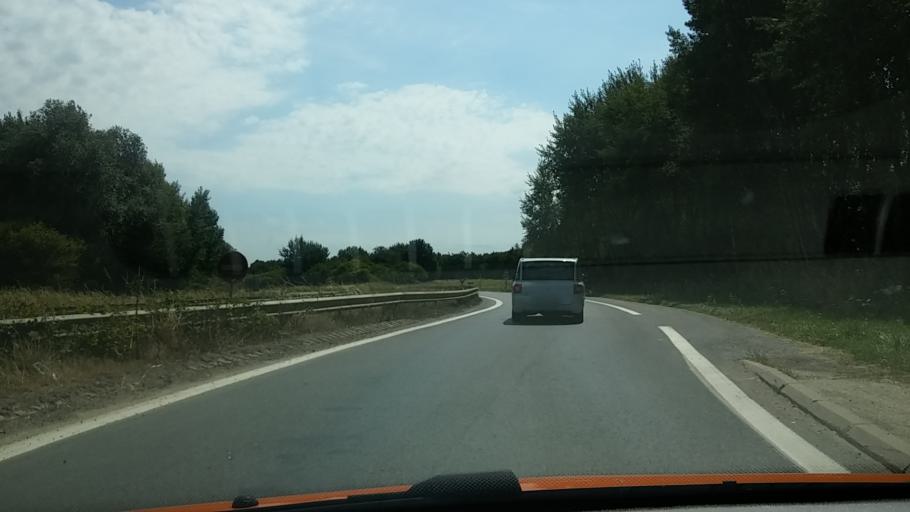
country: FR
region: Ile-de-France
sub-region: Departement de Seine-et-Marne
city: Serris
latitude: 48.8356
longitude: 2.7912
